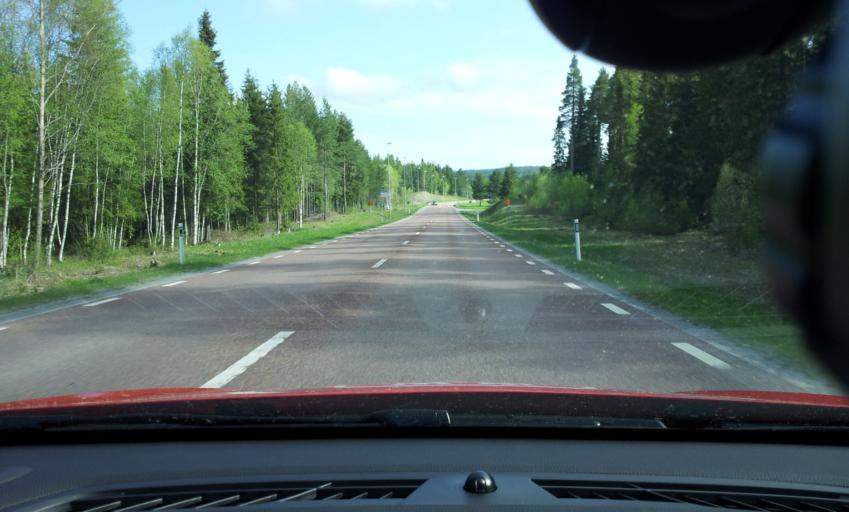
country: SE
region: Jaemtland
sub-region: OEstersunds Kommun
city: Brunflo
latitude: 63.0612
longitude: 14.8348
